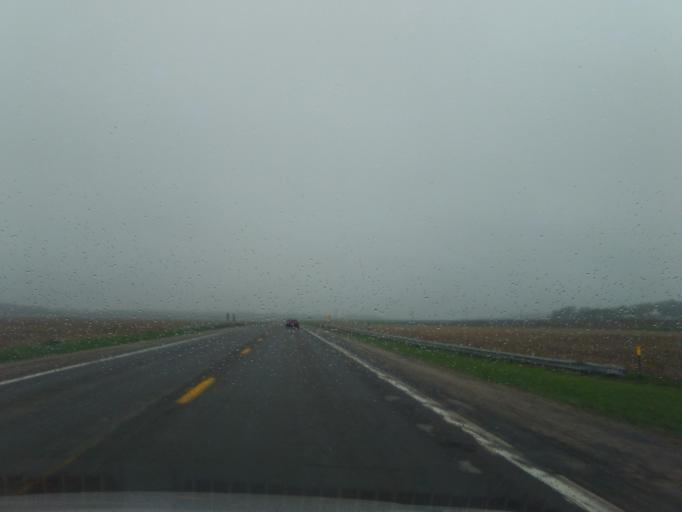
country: US
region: Nebraska
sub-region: Cuming County
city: Wisner
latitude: 41.9578
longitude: -96.8696
